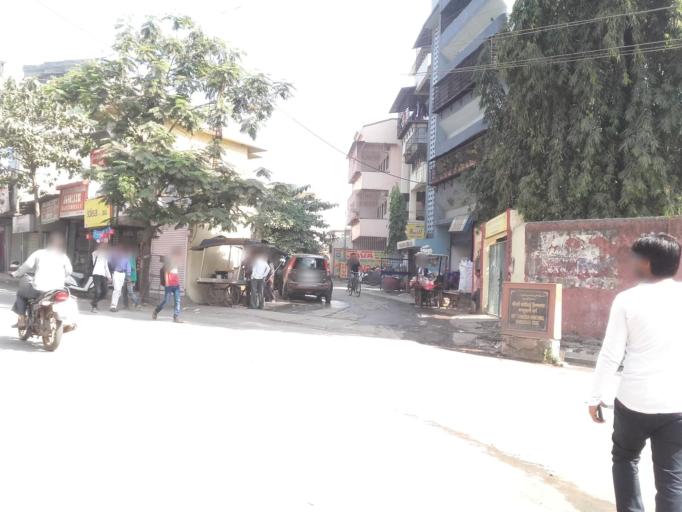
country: IN
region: Maharashtra
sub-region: Thane
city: Ulhasnagar
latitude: 19.2209
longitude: 73.1618
